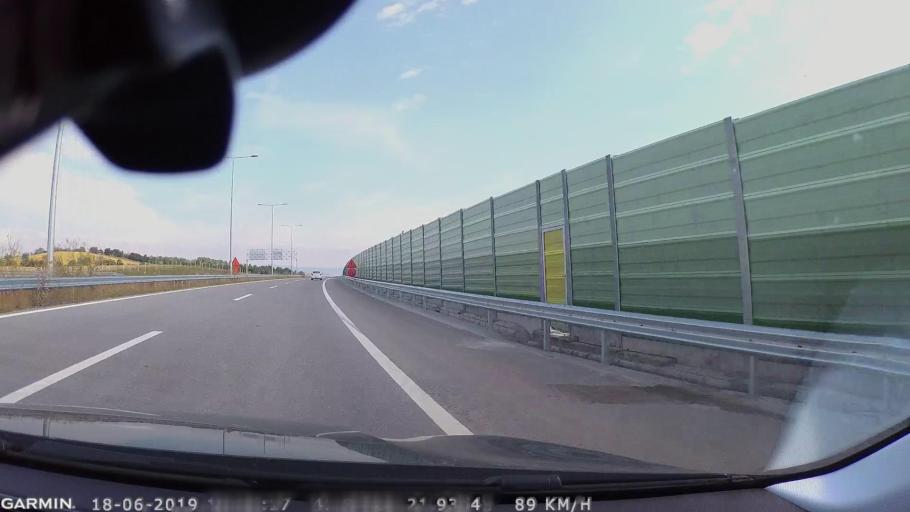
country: MK
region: Sveti Nikole
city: Sveti Nikole
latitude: 41.8797
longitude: 21.9362
